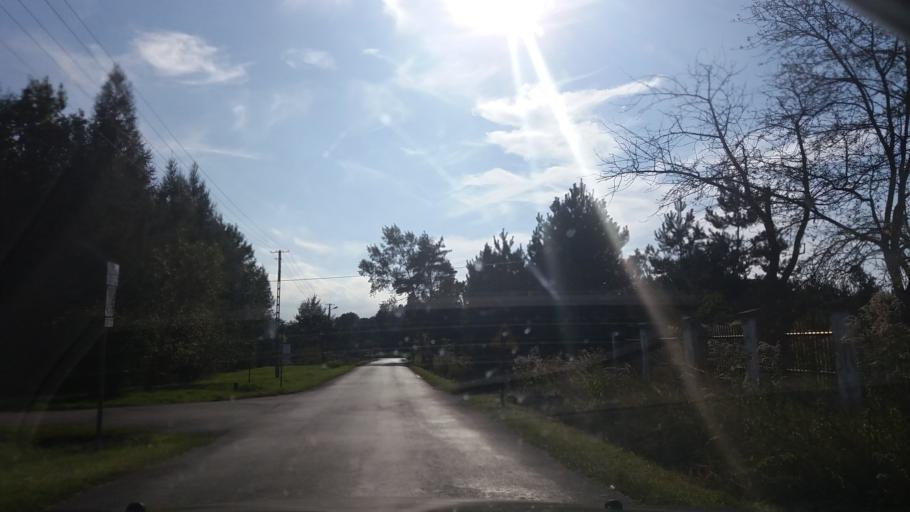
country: PL
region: Lesser Poland Voivodeship
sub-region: Powiat chrzanowski
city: Alwernia
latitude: 50.0433
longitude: 19.5463
